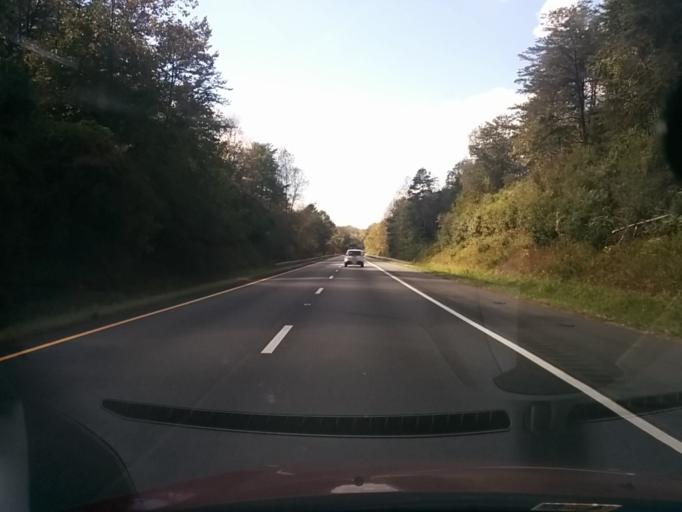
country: US
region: Virginia
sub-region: Albemarle County
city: Crozet
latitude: 38.0315
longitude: -78.6738
